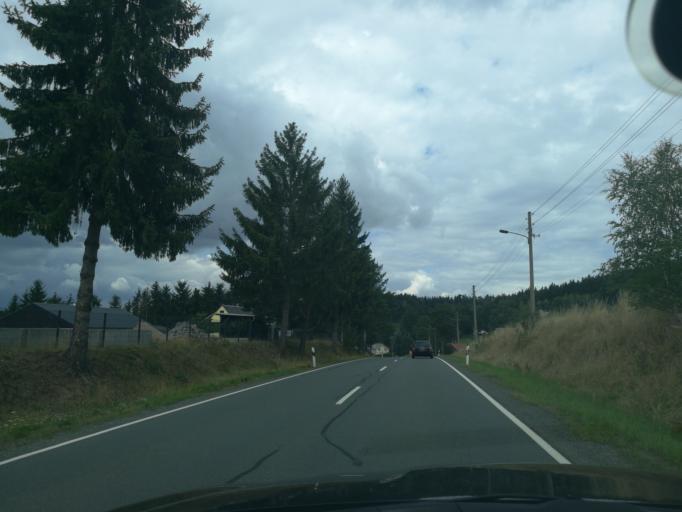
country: DE
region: Saxony
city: Adorf
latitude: 50.3615
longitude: 12.2248
